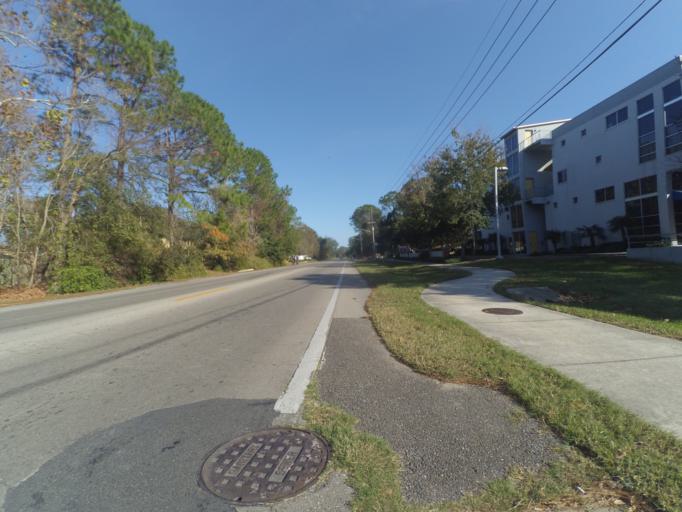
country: US
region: Florida
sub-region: Alachua County
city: Gainesville
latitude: 29.6199
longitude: -82.3606
